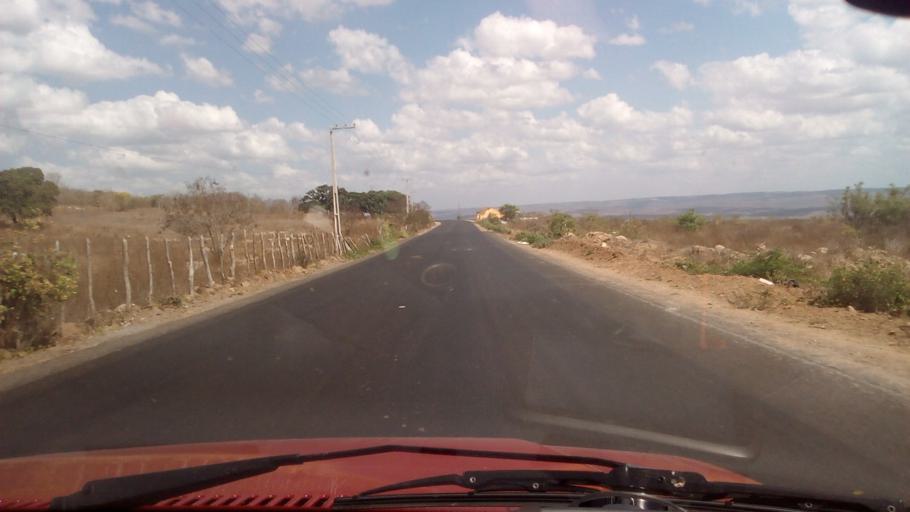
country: BR
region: Paraiba
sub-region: Cacimba De Dentro
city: Cacimba de Dentro
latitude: -6.6485
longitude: -35.7830
